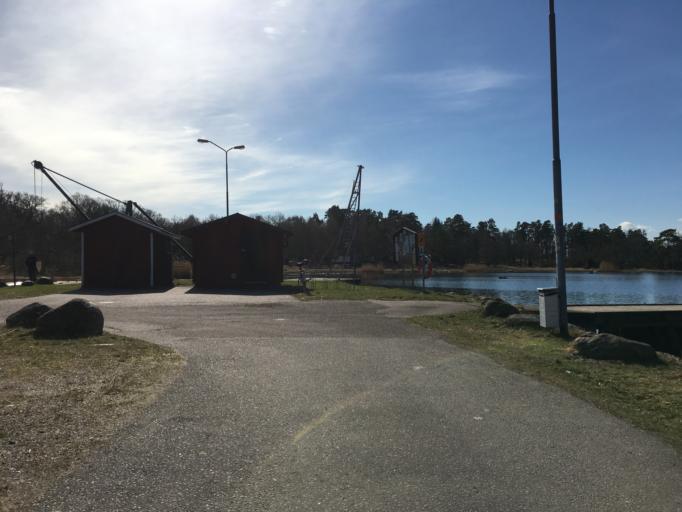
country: SE
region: Kalmar
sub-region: Kalmar Kommun
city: Kalmar
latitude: 56.6514
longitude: 16.3253
